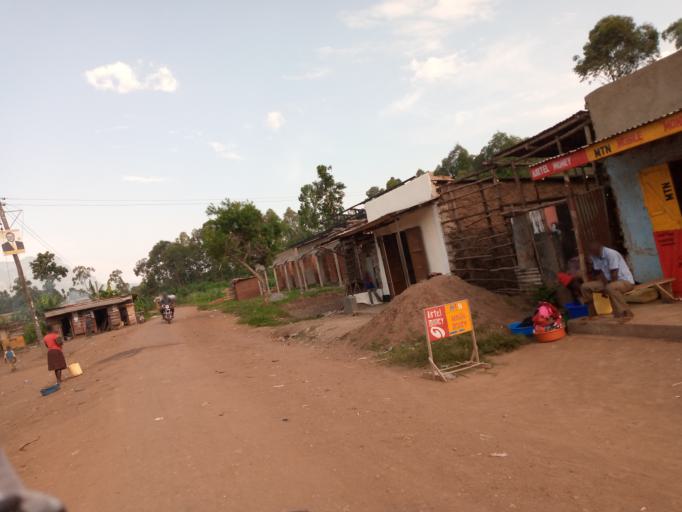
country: UG
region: Eastern Region
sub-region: Mbale District
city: Mbale
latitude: 1.0560
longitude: 34.1614
